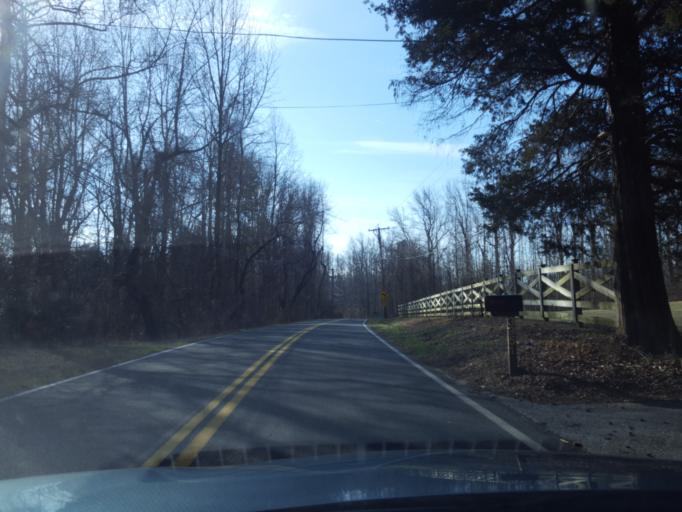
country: US
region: Maryland
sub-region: Calvert County
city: Chesapeake Beach
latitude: 38.6237
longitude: -76.5321
